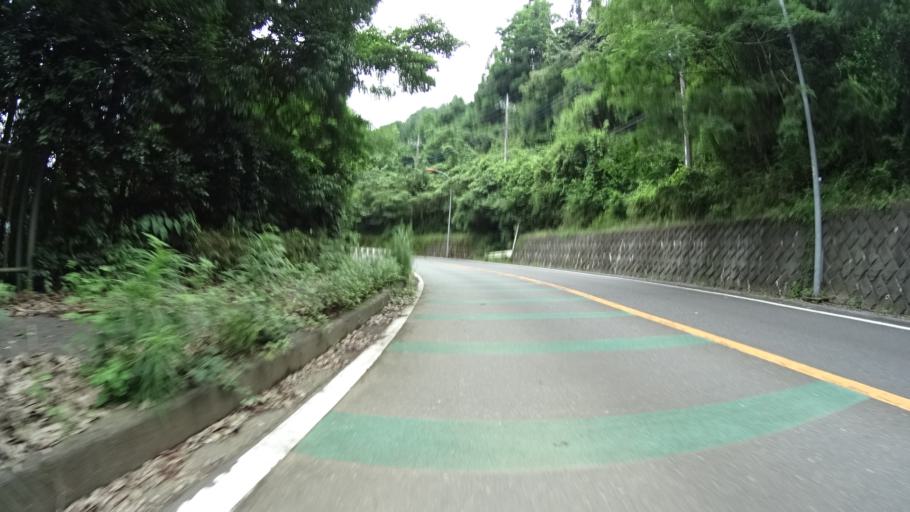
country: JP
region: Kanagawa
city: Hadano
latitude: 35.5179
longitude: 139.2312
